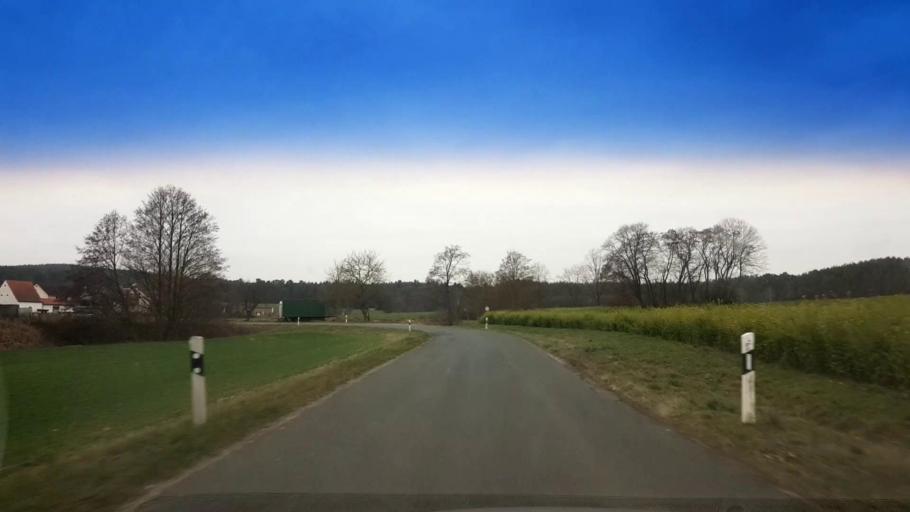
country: DE
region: Bavaria
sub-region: Upper Franconia
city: Pettstadt
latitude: 49.7784
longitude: 10.9145
